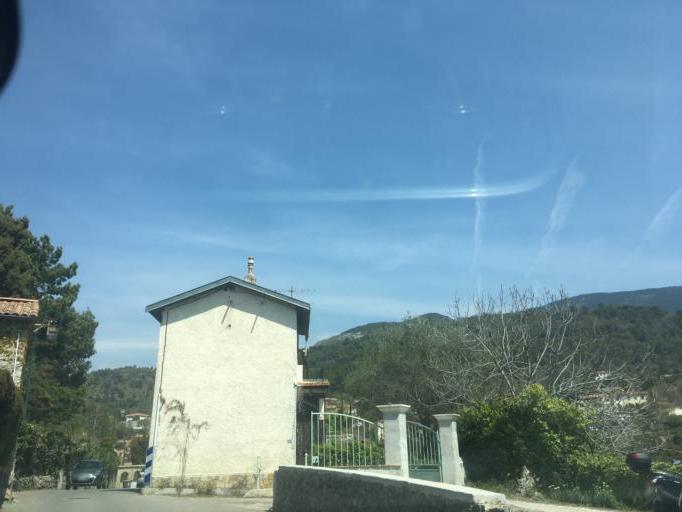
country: FR
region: Provence-Alpes-Cote d'Azur
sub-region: Departement des Alpes-Maritimes
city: Levens
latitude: 43.8535
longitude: 7.2284
